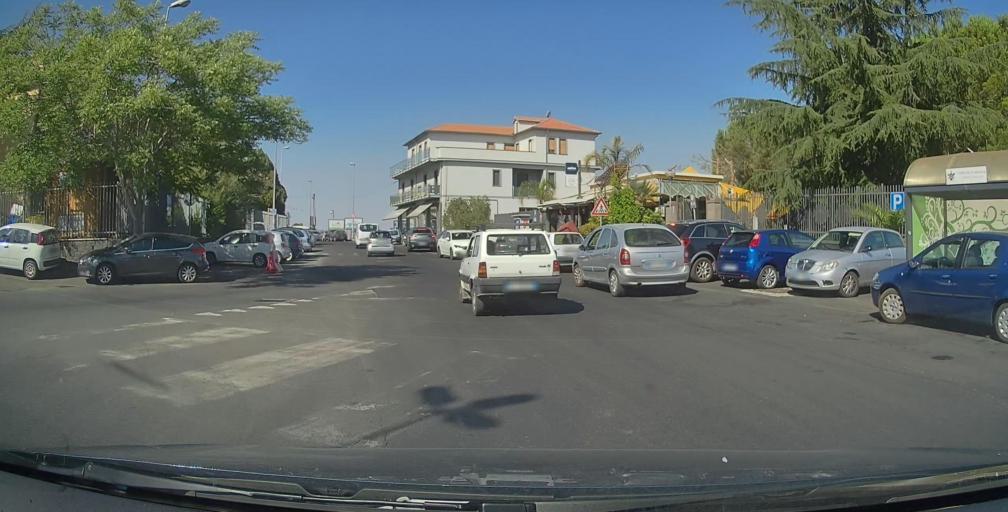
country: IT
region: Sicily
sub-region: Catania
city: Bronte
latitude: 37.7838
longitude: 14.8262
